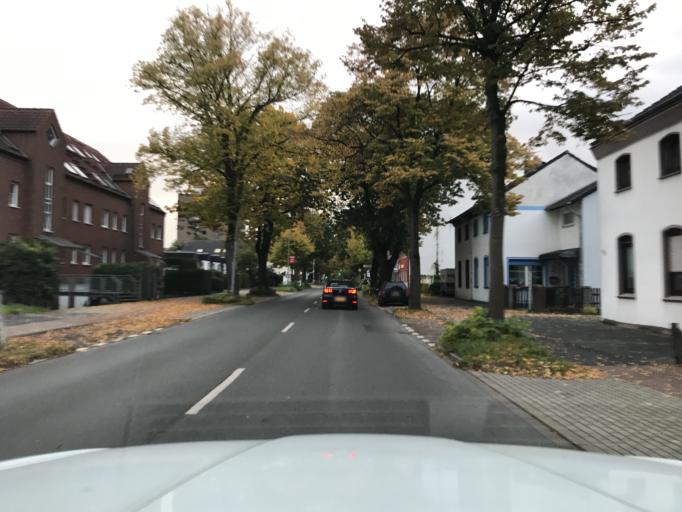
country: DE
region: North Rhine-Westphalia
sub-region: Regierungsbezirk Dusseldorf
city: Hochfeld
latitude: 51.3746
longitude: 6.7805
